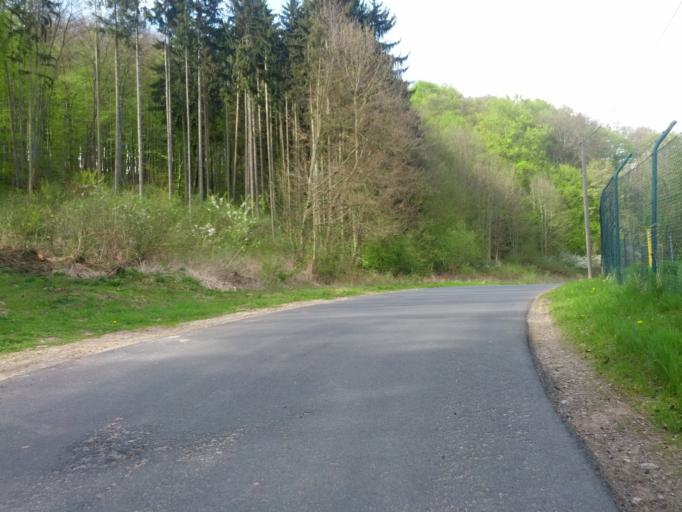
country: DE
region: Thuringia
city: Krauthausen
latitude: 50.9982
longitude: 10.2394
